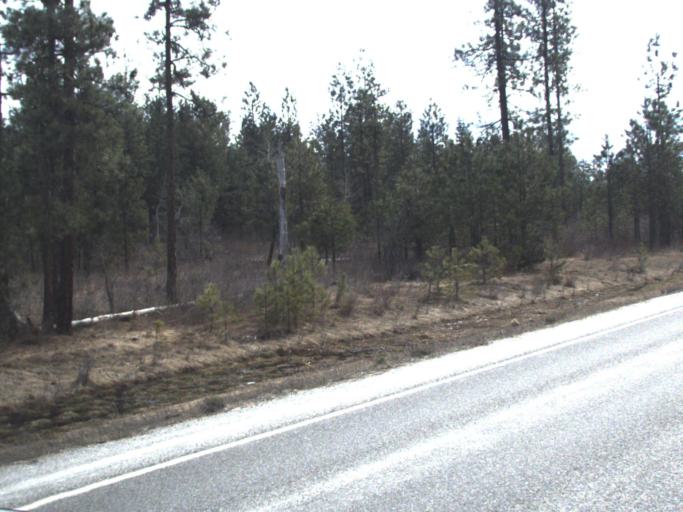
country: US
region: Washington
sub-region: Pend Oreille County
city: Newport
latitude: 48.3185
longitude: -117.2929
